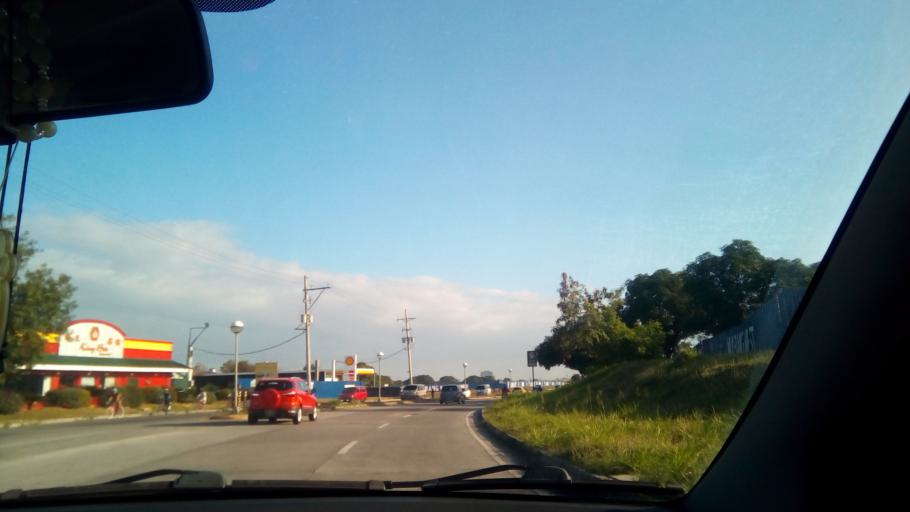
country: PH
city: Sambayanihan People's Village
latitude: 14.4064
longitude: 121.0120
